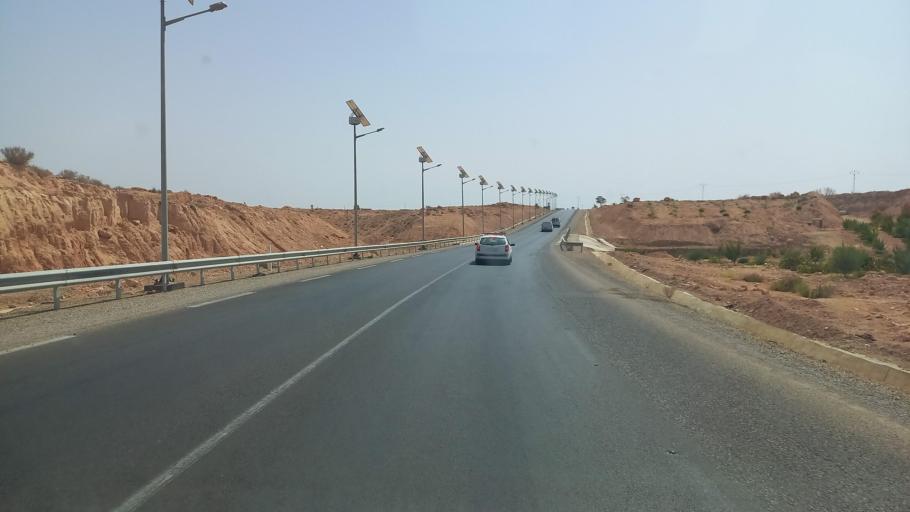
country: TN
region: Madanin
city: Medenine
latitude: 33.3703
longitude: 10.6770
